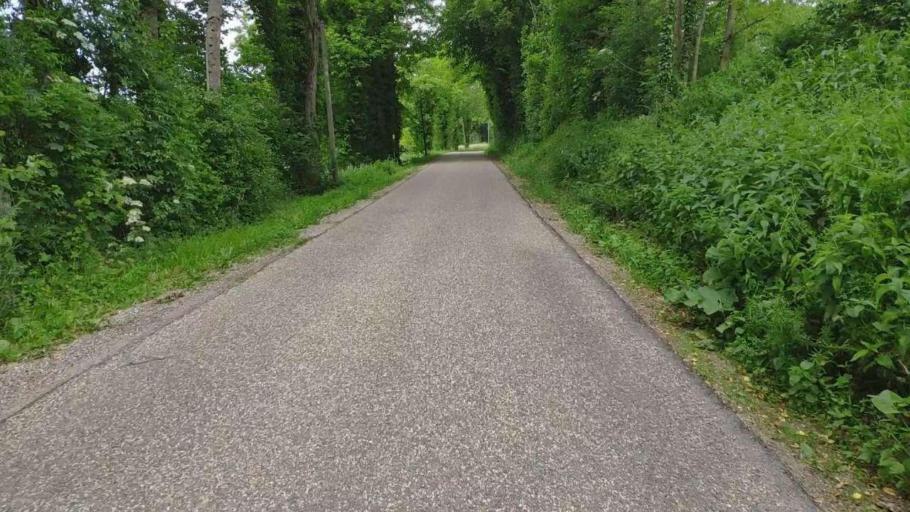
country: FR
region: Franche-Comte
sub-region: Departement du Jura
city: Montmorot
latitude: 46.7560
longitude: 5.5415
